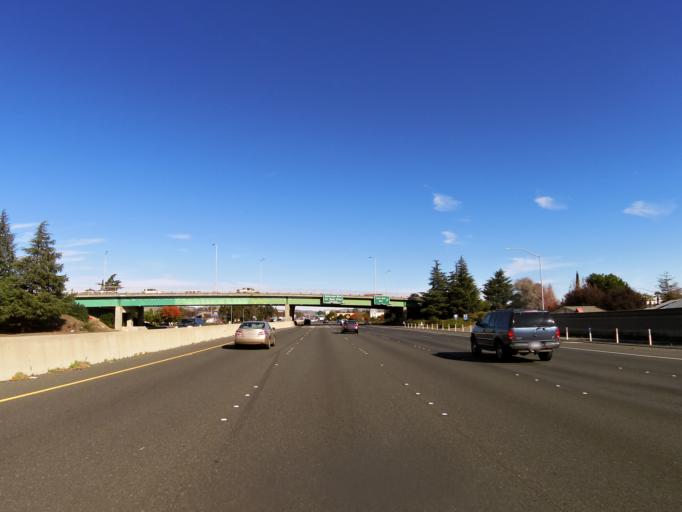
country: US
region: California
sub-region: Solano County
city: Fairfield
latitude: 38.2572
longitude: -122.0633
